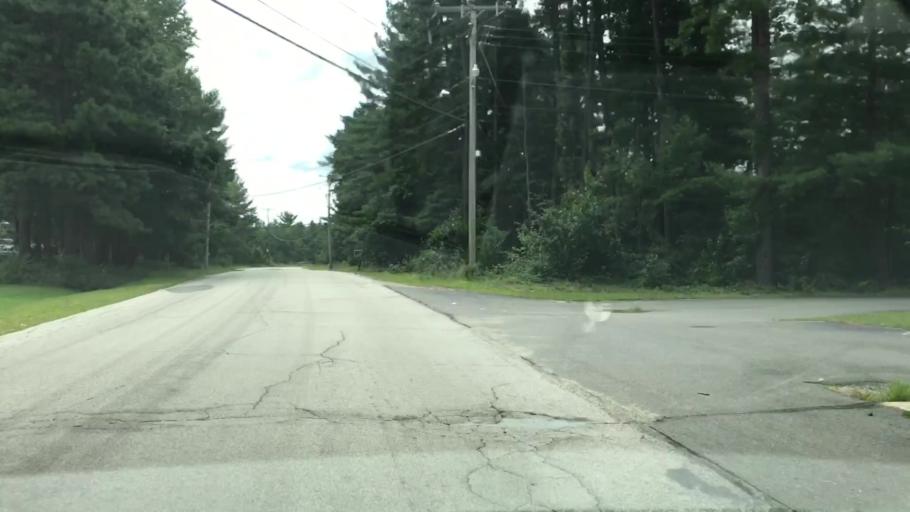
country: US
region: New Hampshire
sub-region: Hillsborough County
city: Hollis
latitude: 42.8088
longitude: -71.5830
